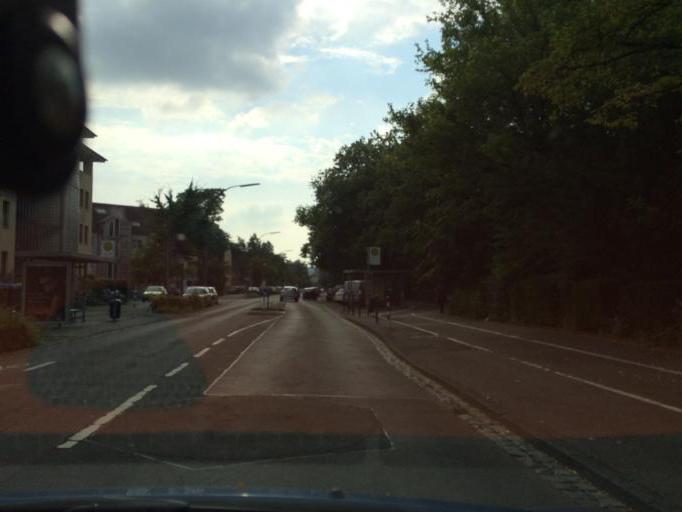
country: DE
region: North Rhine-Westphalia
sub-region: Regierungsbezirk Koln
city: Konigswinter
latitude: 50.6956
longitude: 7.1552
